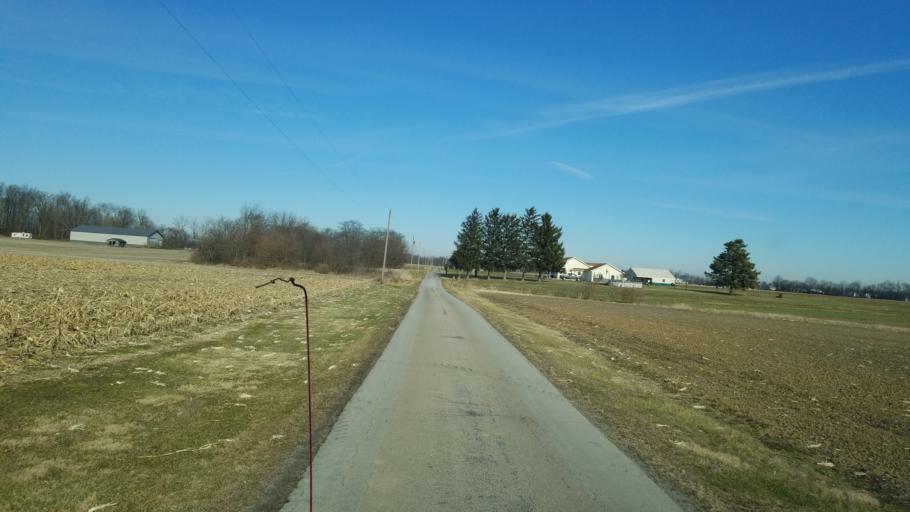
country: US
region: Ohio
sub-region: Putnam County
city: Pandora
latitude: 40.9990
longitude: -83.9378
